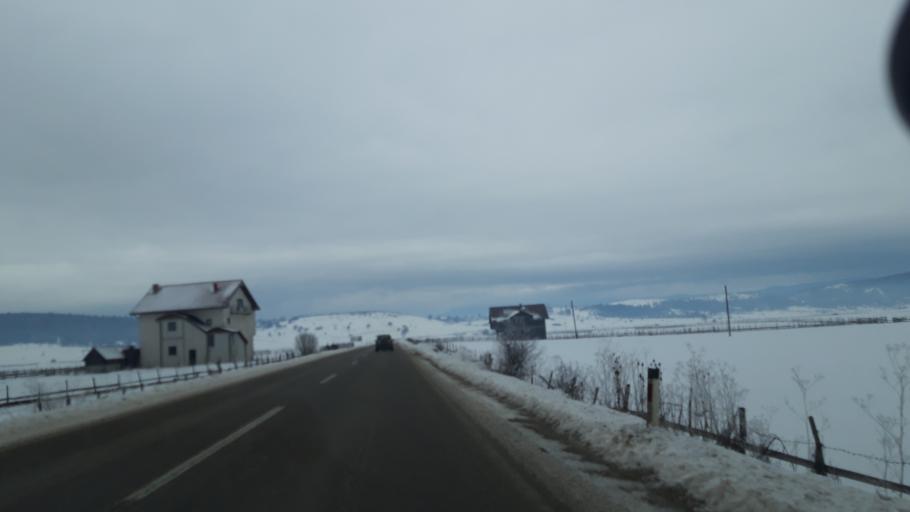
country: BA
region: Republika Srpska
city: Sokolac
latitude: 43.9602
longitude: 18.8552
